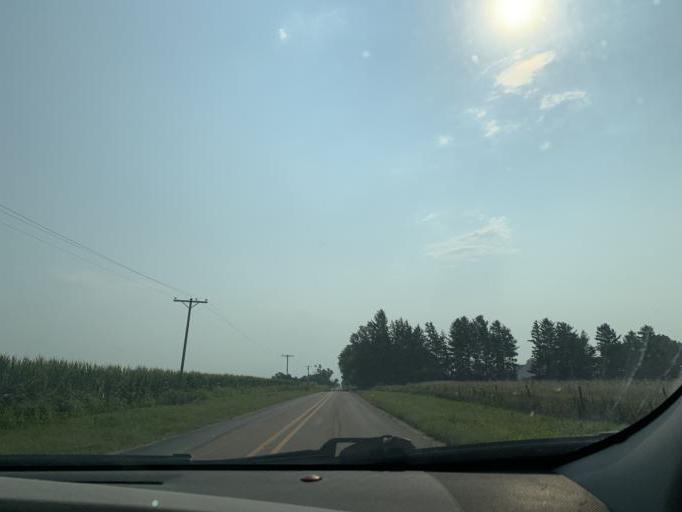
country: US
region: Illinois
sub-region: Whiteside County
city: Morrison
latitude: 41.8480
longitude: -89.8644
